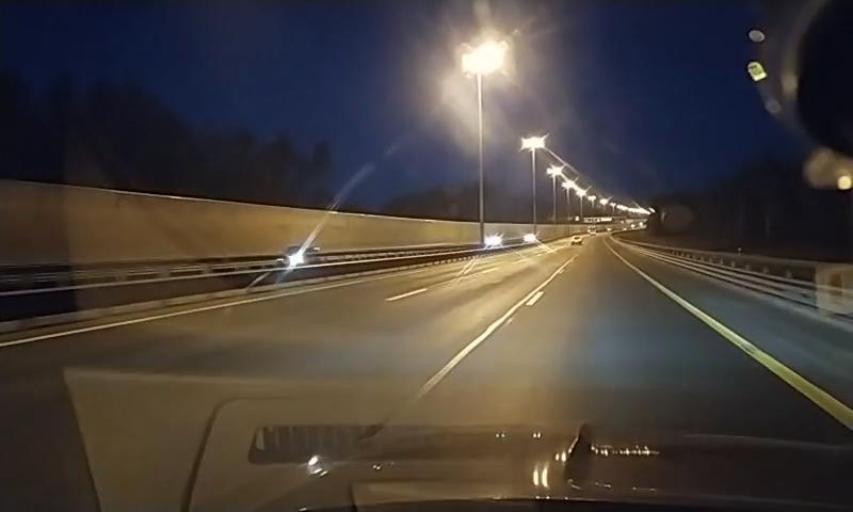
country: RU
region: St.-Petersburg
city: Beloostrov
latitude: 60.1165
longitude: 30.0771
